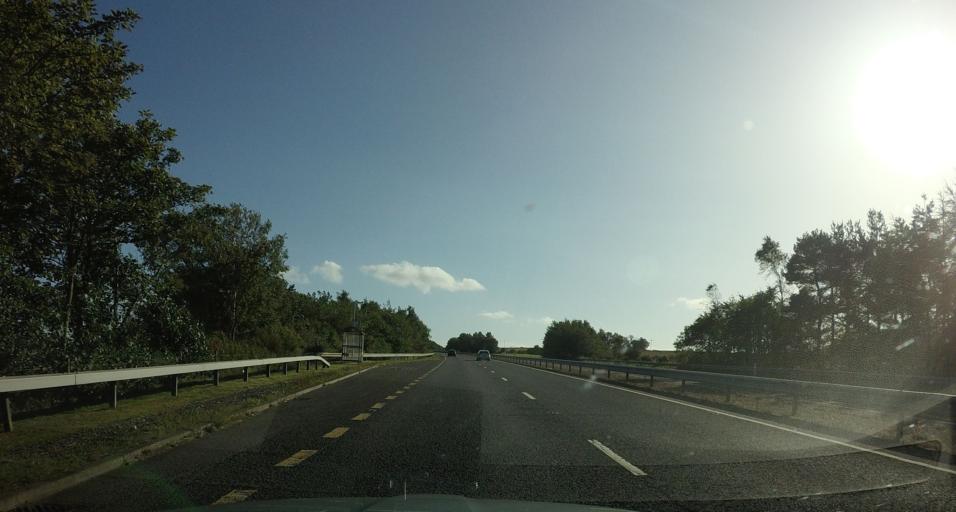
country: GB
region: Scotland
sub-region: Angus
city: Forfar
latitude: 56.5865
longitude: -2.9133
